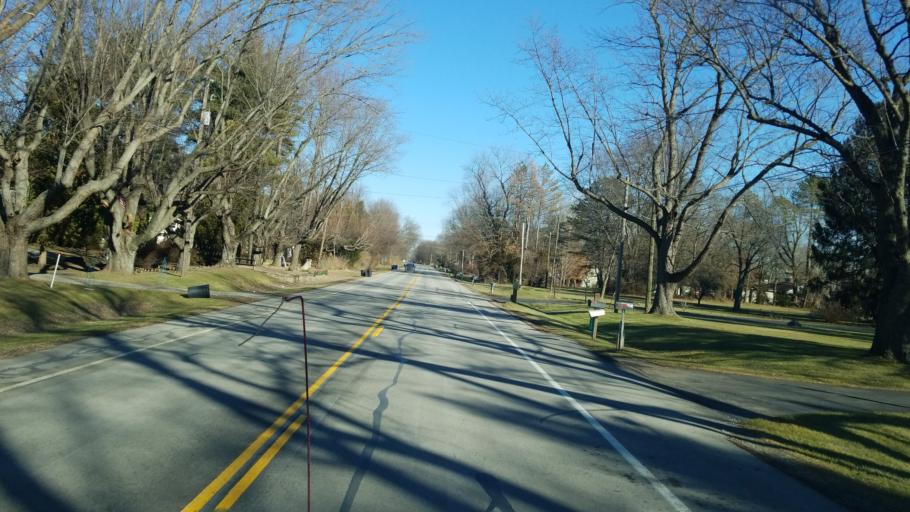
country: US
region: Ohio
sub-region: Lucas County
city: Waterville
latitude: 41.4687
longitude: -83.7609
